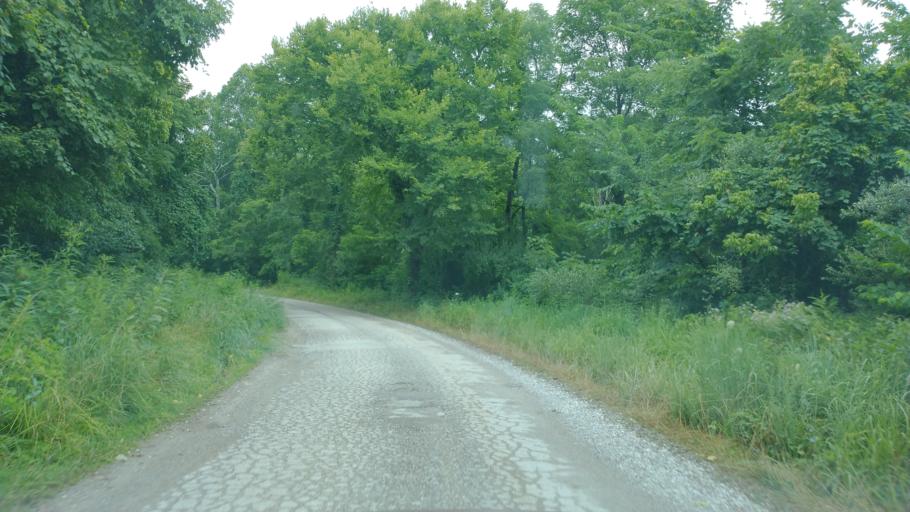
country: US
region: Ohio
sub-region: Meigs County
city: Middleport
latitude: 38.9315
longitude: -82.0698
